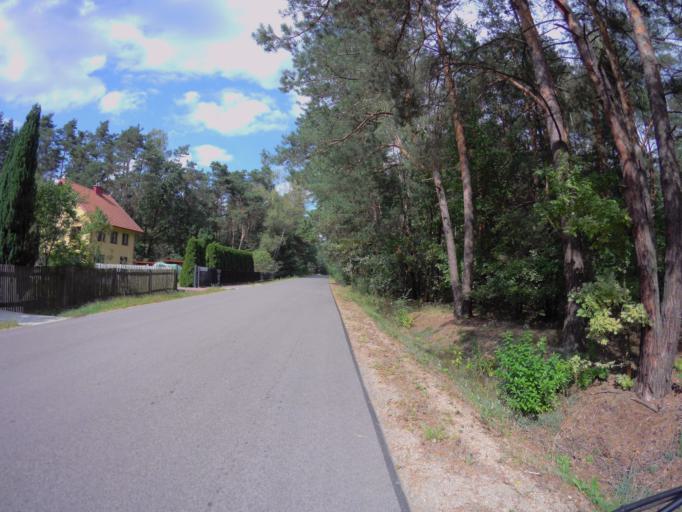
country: PL
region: Subcarpathian Voivodeship
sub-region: Powiat lezajski
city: Brzoza Krolewska
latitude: 50.2752
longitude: 22.3527
